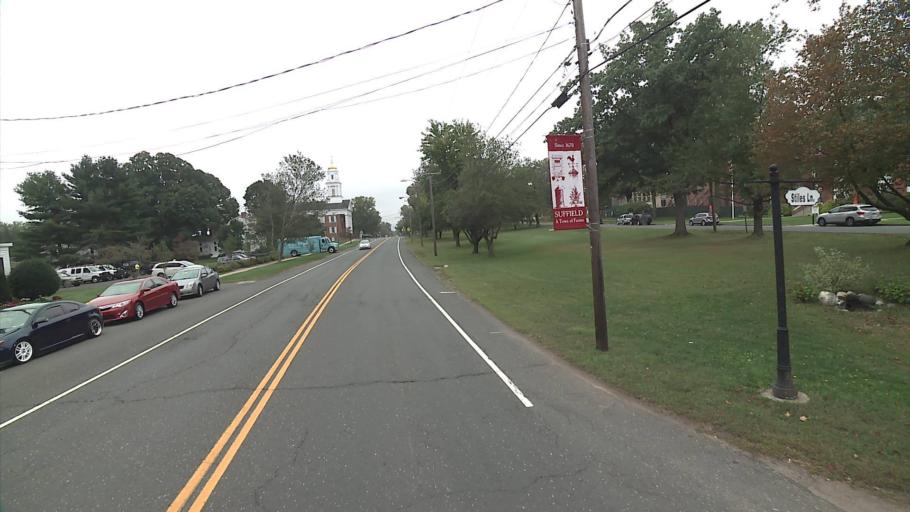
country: US
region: Connecticut
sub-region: Hartford County
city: Suffield Depot
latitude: 41.9856
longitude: -72.6498
